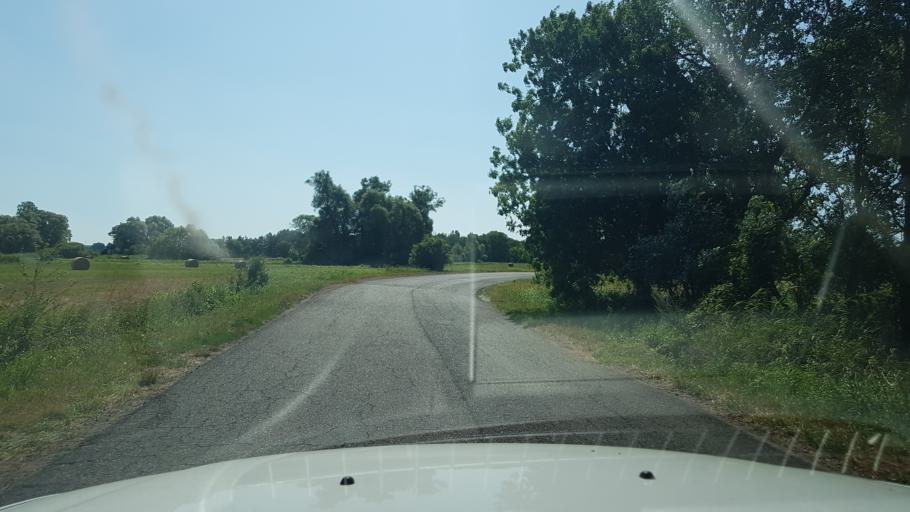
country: PL
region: West Pomeranian Voivodeship
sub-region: Powiat goleniowski
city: Goleniow
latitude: 53.4773
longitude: 14.7122
